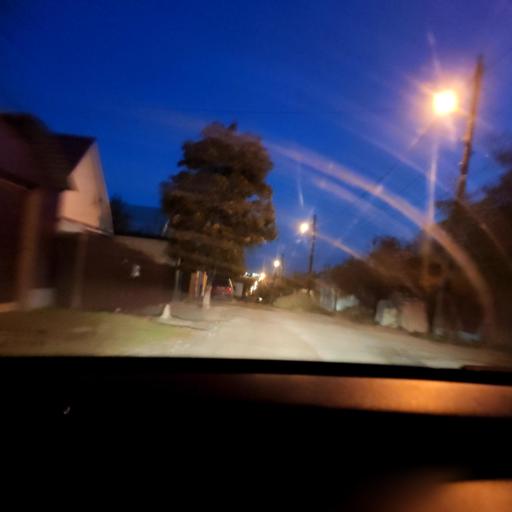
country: RU
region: Samara
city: Samara
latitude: 53.1788
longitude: 50.1759
